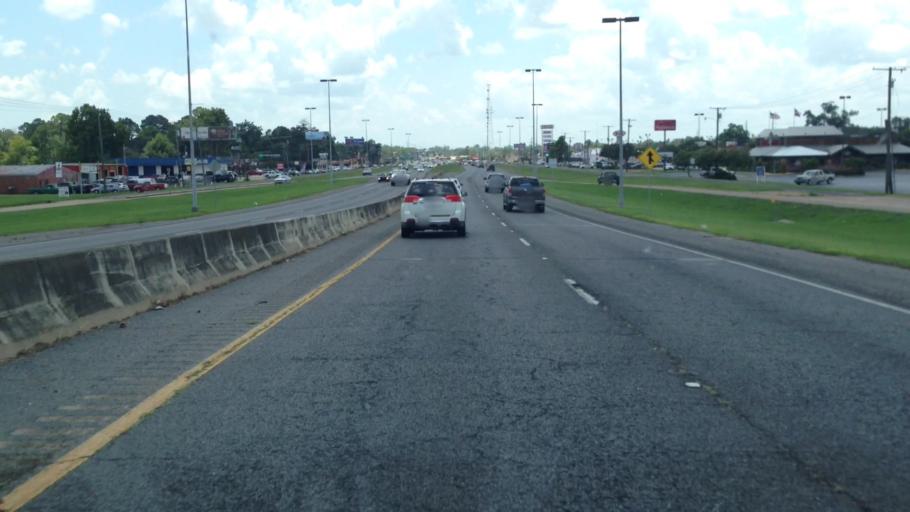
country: US
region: Louisiana
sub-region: Rapides Parish
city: Alexandria
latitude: 31.2849
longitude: -92.4743
